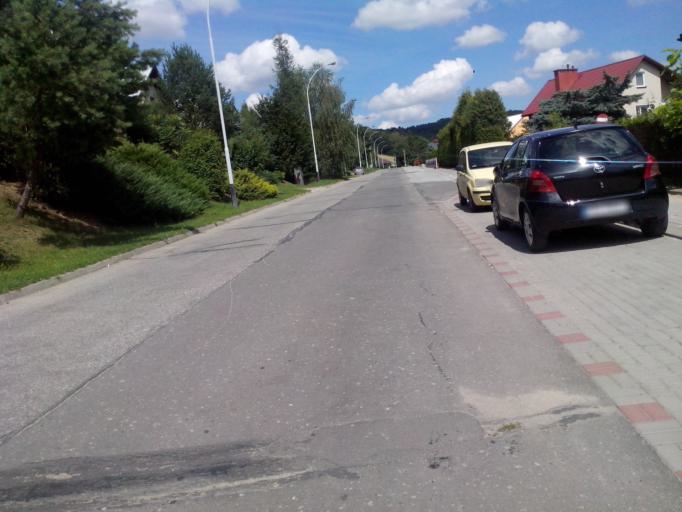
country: PL
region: Subcarpathian Voivodeship
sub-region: Powiat strzyzowski
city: Strzyzow
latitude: 49.8727
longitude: 21.7871
